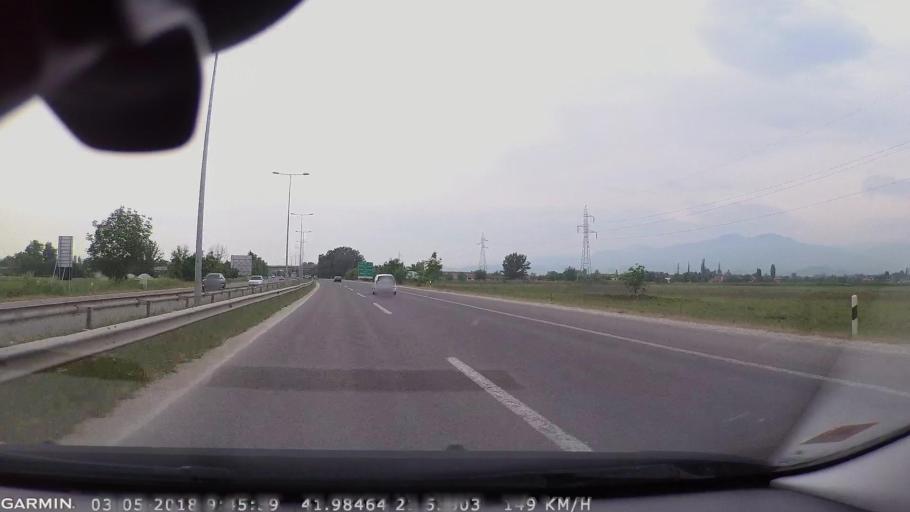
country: MK
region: Ilinden
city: Jurumleri
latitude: 41.9831
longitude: 21.5392
